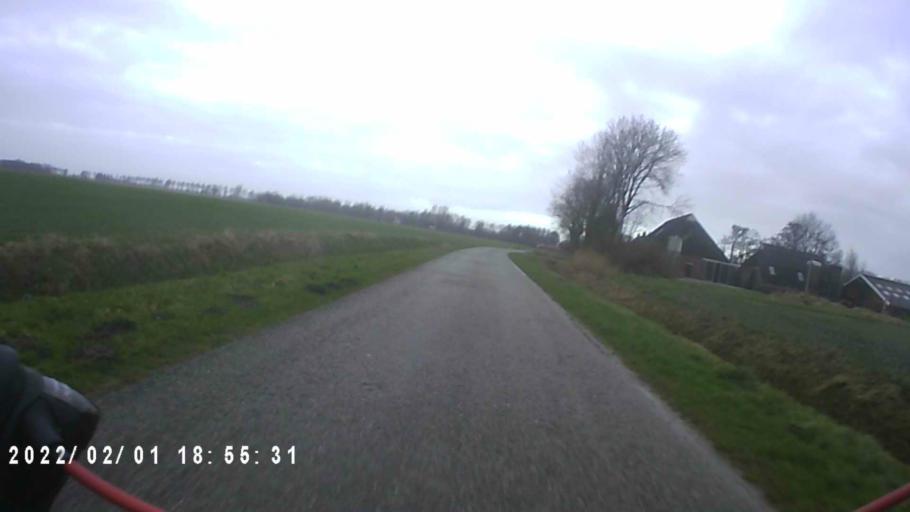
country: NL
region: Groningen
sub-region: Gemeente Zuidhorn
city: Oldehove
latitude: 53.3535
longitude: 6.4137
